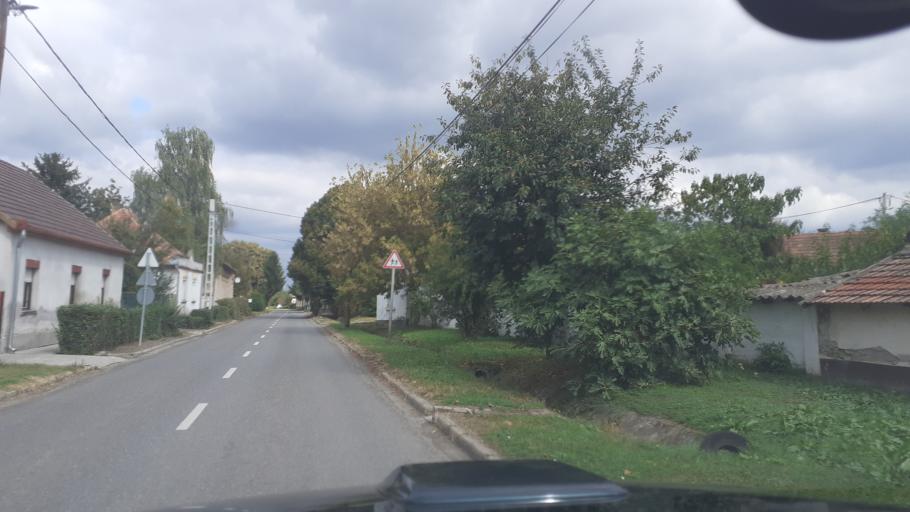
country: HU
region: Bacs-Kiskun
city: Apostag
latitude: 46.8811
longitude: 18.9644
